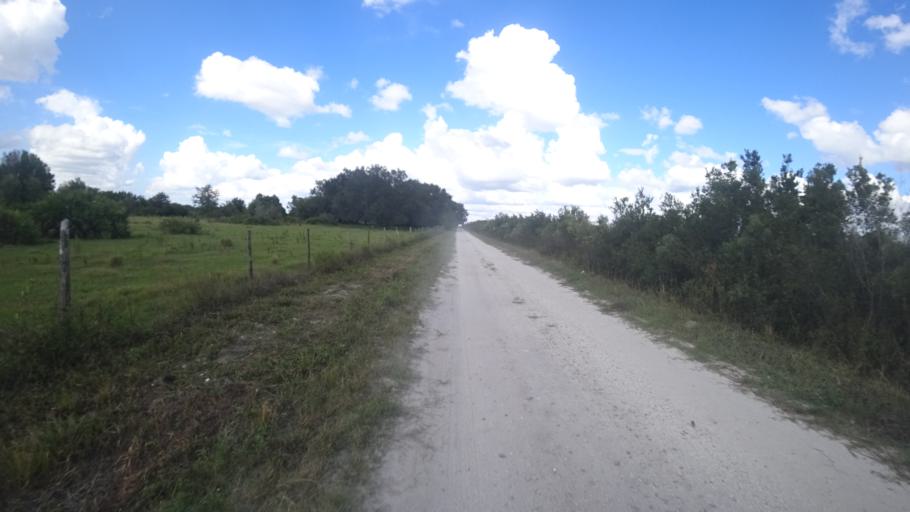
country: US
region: Florida
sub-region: DeSoto County
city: Arcadia
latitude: 27.3340
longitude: -82.1050
